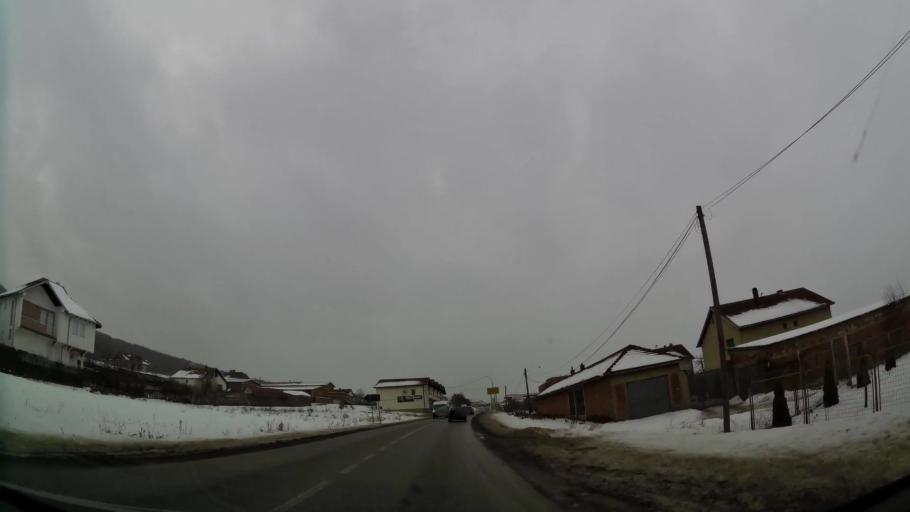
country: XK
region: Pristina
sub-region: Komuna e Prishtines
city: Pristina
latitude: 42.7294
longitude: 21.1435
